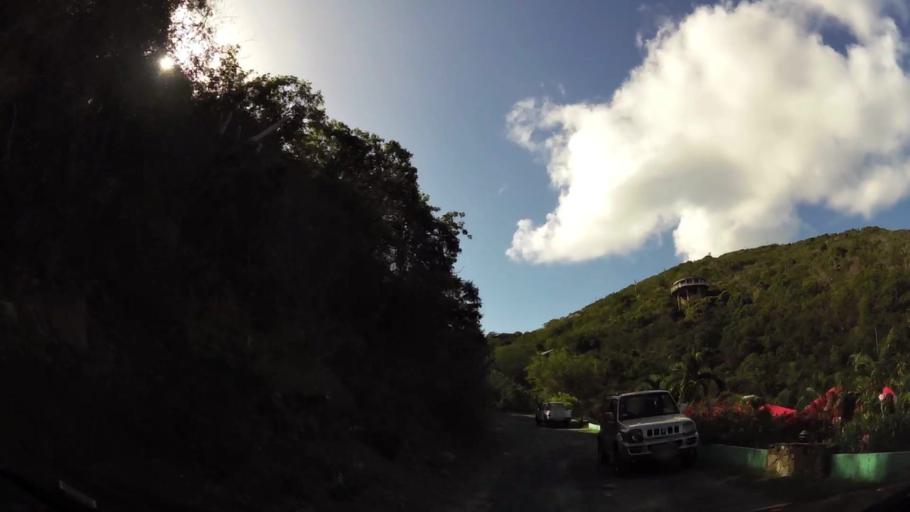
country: VG
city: Tortola
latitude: 18.4967
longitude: -64.3853
